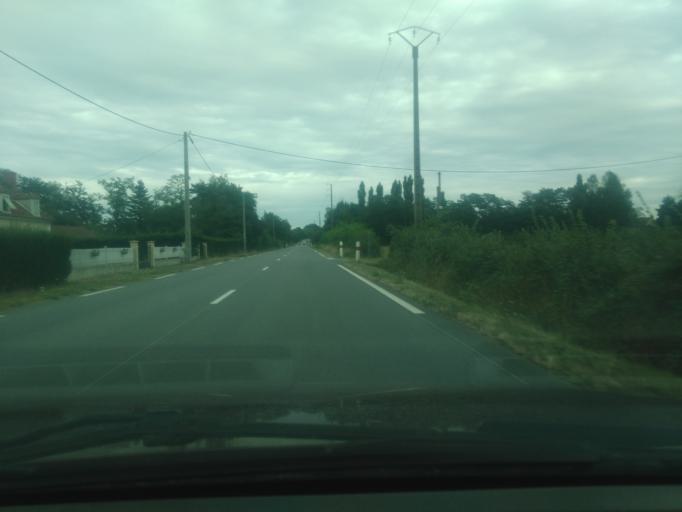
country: FR
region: Auvergne
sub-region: Departement de l'Allier
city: Ainay-le-Chateau
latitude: 46.7382
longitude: 2.6932
